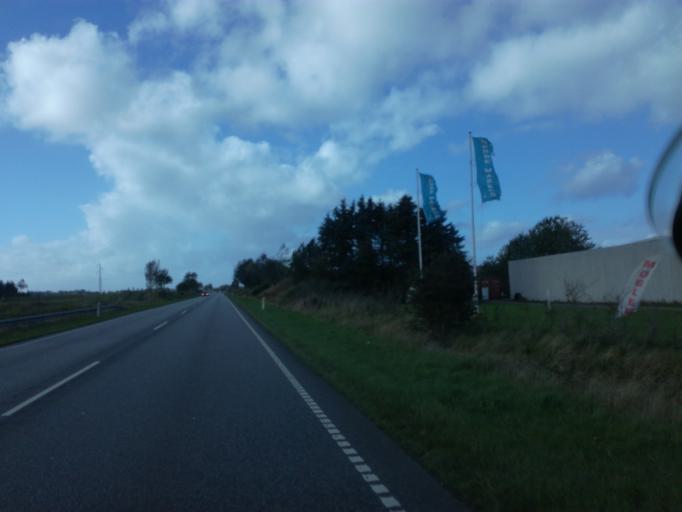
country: DK
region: South Denmark
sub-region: Vejle Kommune
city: Brejning
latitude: 55.6271
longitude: 9.7177
